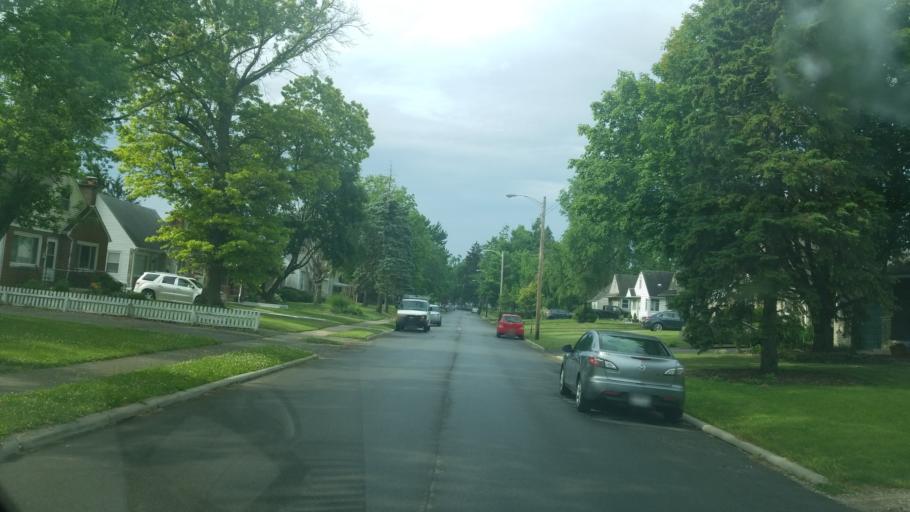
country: US
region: Ohio
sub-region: Franklin County
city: Minerva Park
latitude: 40.0296
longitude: -82.9722
